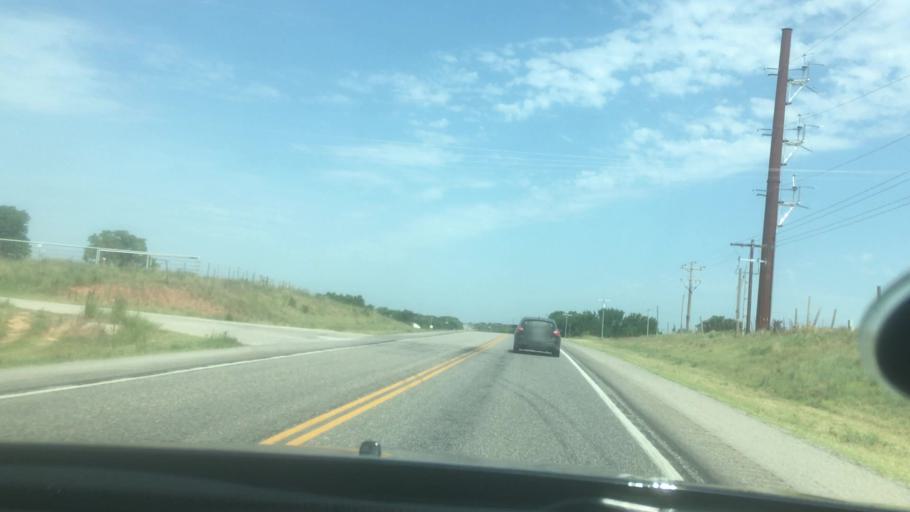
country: US
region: Oklahoma
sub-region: Seminole County
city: Konawa
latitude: 34.8668
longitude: -96.8335
